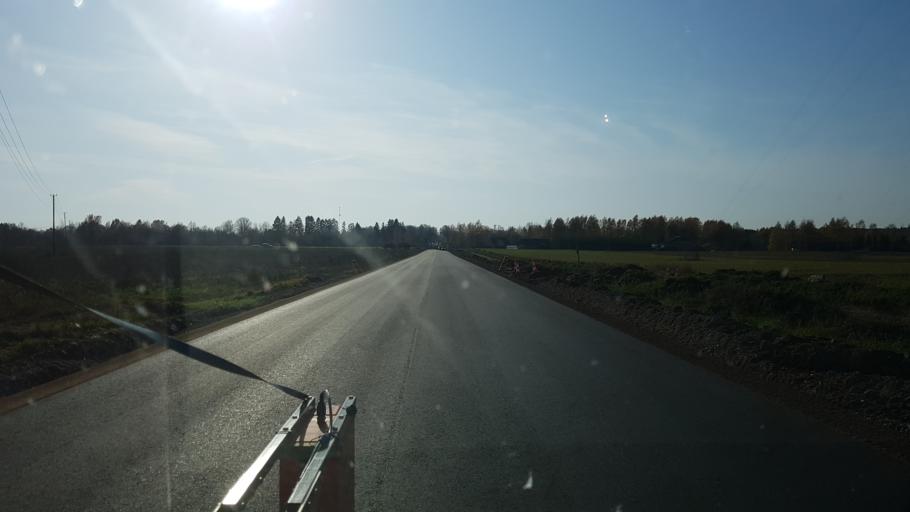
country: EE
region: Vorumaa
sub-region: Antsla vald
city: Vana-Antsla
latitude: 57.8378
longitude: 26.5460
